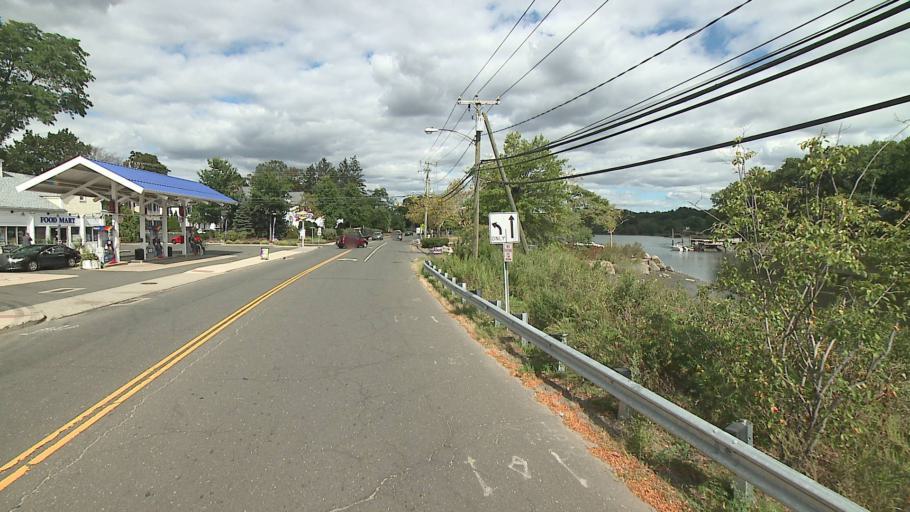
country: US
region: Connecticut
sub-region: Fairfield County
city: Westport
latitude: 41.1321
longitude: -73.3678
